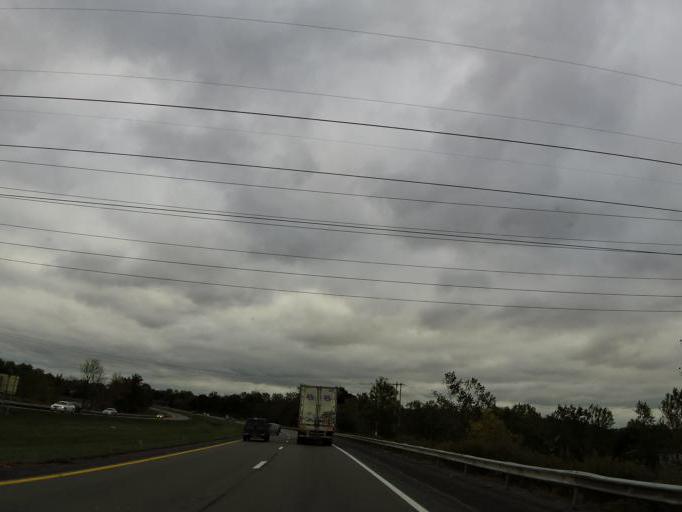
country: US
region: New York
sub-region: Erie County
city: West Seneca
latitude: 42.8444
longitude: -78.7732
